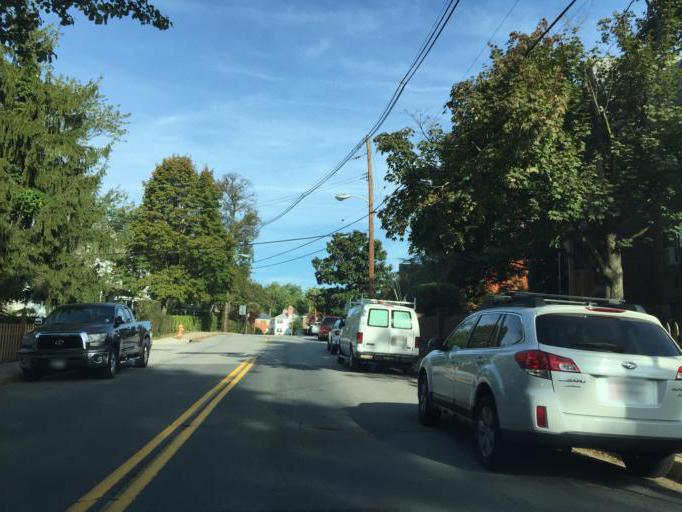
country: US
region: Maryland
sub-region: Baltimore County
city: Towson
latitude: 39.3622
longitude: -76.6128
